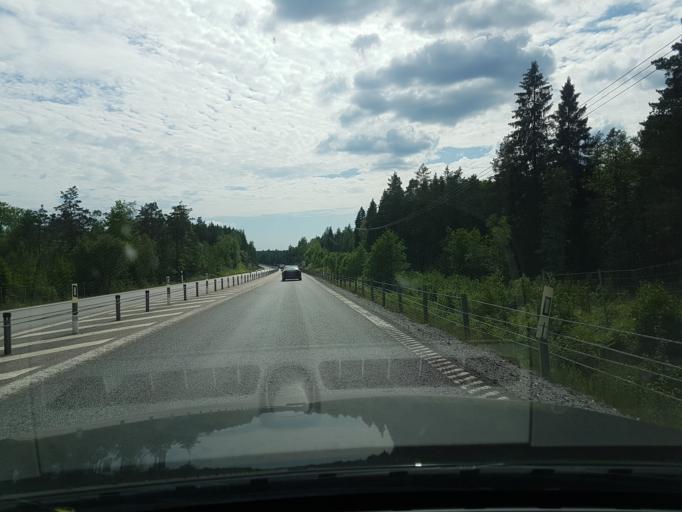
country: SE
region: Stockholm
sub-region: Osterakers Kommun
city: Akersberga
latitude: 59.5798
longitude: 18.2446
